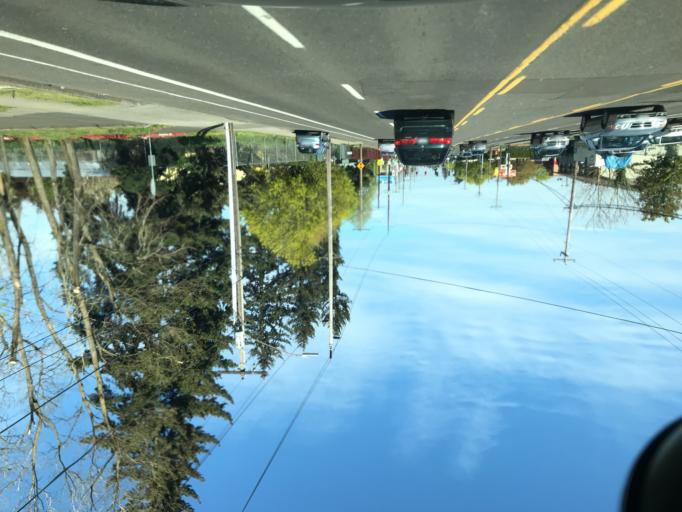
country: US
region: Oregon
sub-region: Clackamas County
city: Happy Valley
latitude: 45.5043
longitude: -122.5082
